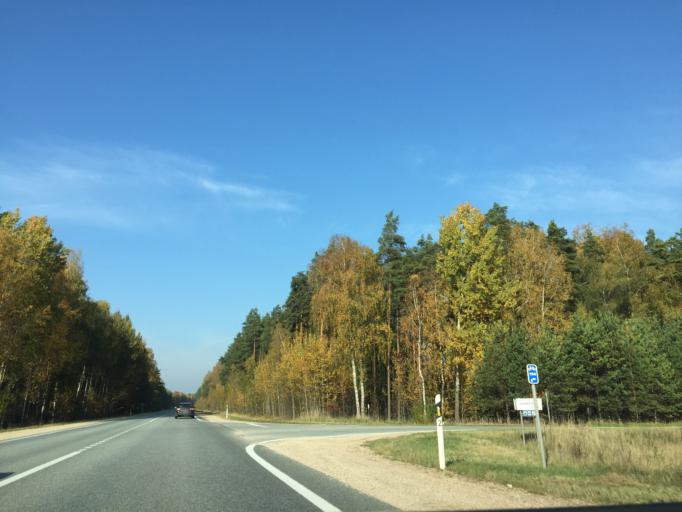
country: LV
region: Babite
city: Pinki
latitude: 56.8935
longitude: 23.9330
